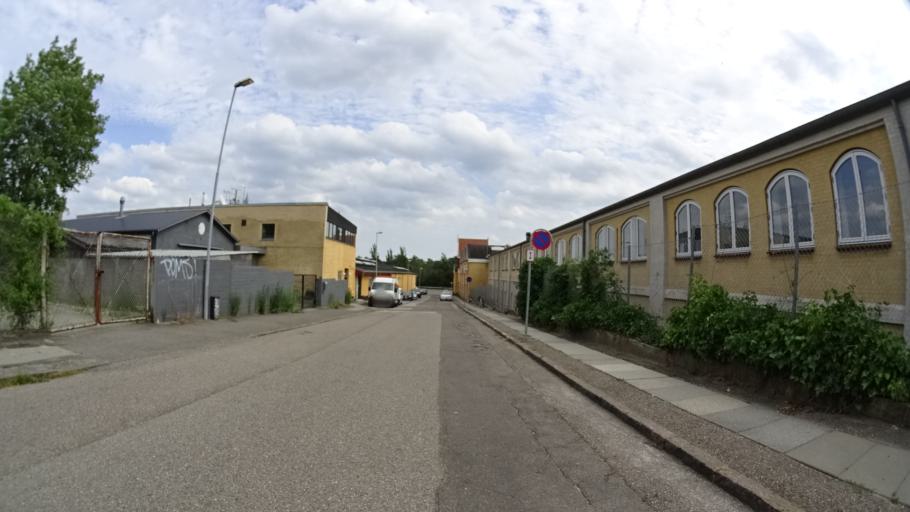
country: DK
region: Central Jutland
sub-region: Arhus Kommune
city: Arhus
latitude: 56.1540
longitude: 10.1774
